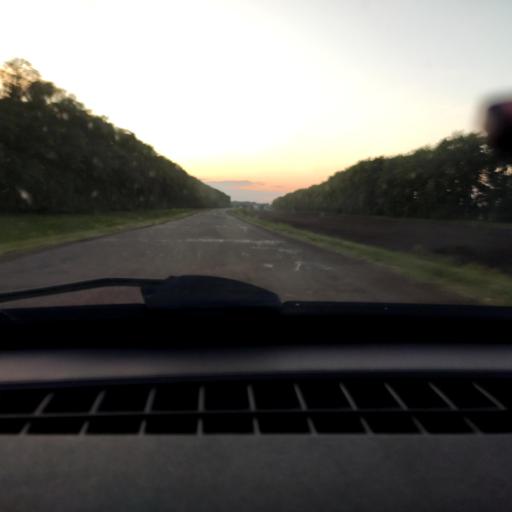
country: RU
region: Bashkortostan
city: Karmaskaly
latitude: 54.3904
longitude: 56.1742
